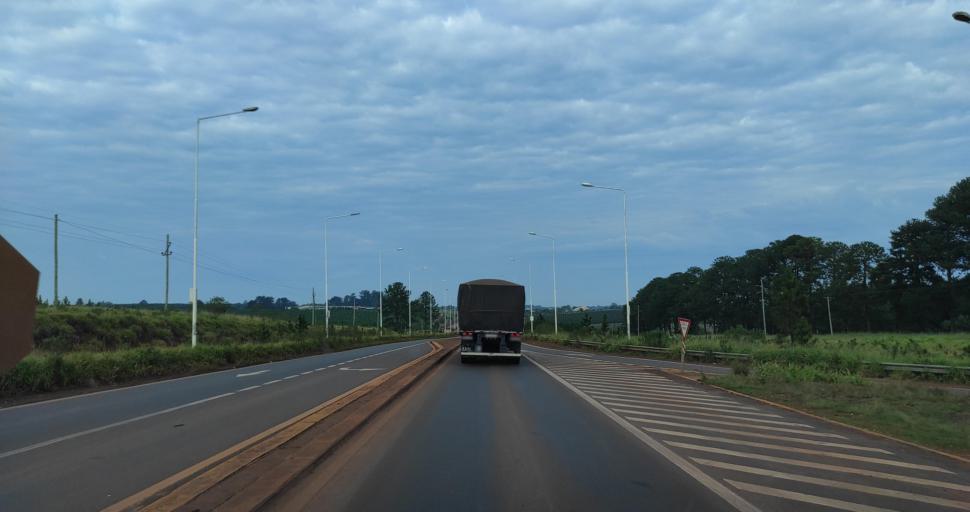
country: AR
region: Corrientes
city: Gobernador Ingeniero Valentin Virasoro
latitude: -27.9675
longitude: -56.0086
